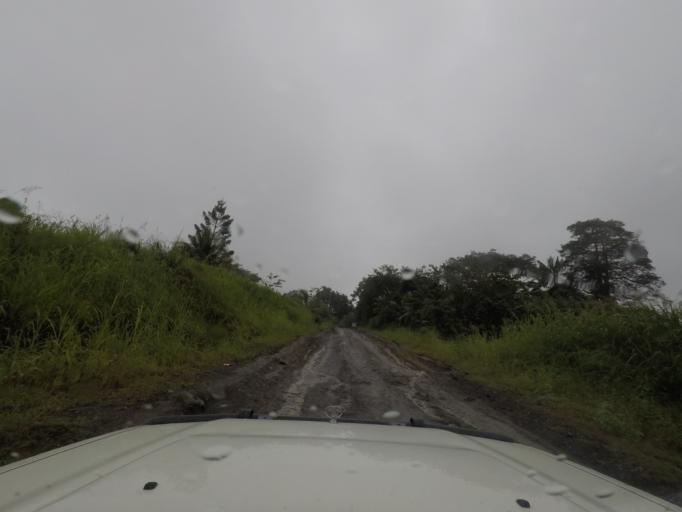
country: PG
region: Madang
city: Madang
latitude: -5.4674
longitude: 145.4879
